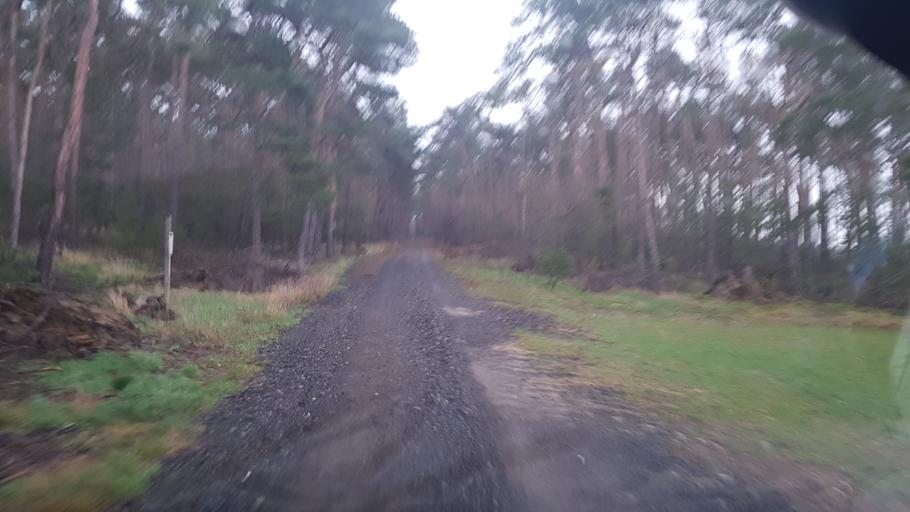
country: DE
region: Brandenburg
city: Muhlberg
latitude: 51.4983
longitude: 13.2931
